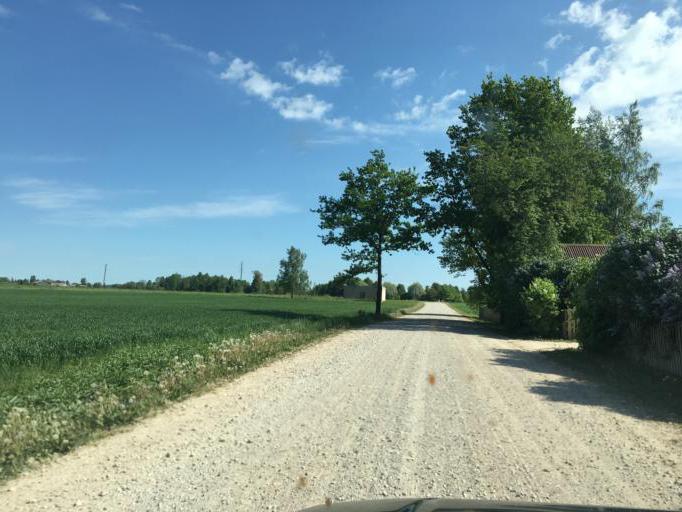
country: LV
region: Talsu Rajons
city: Valdemarpils
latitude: 57.3399
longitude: 22.4848
